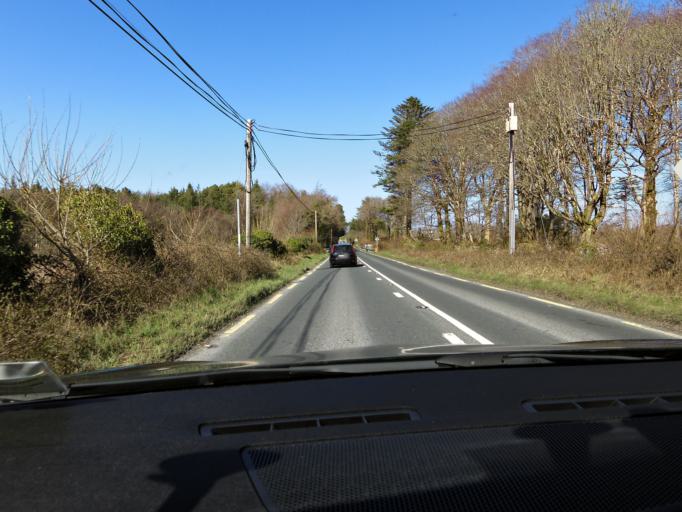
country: IE
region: Connaught
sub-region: County Galway
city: Moycullen
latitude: 53.3808
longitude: -9.2498
